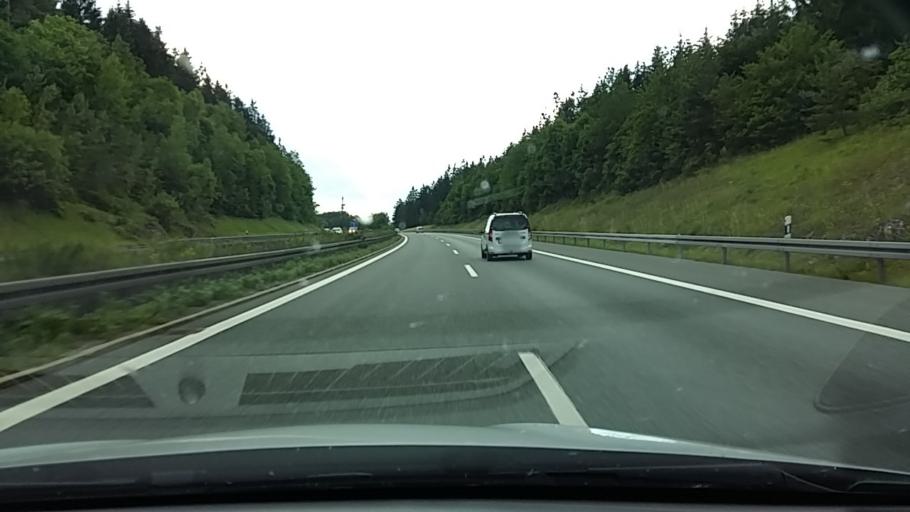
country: DE
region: Bavaria
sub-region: Upper Palatinate
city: Illschwang
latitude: 49.4215
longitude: 11.7102
